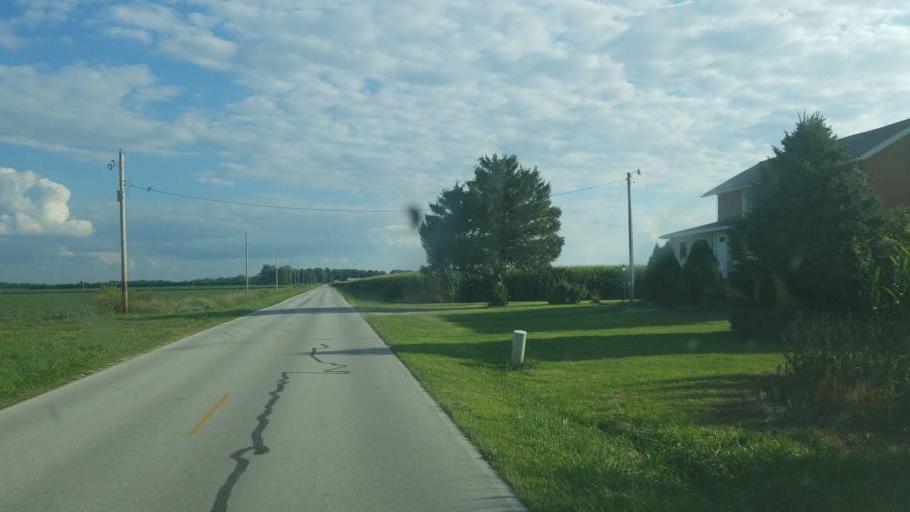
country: US
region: Ohio
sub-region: Sandusky County
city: Green Springs
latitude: 41.2385
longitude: -83.1311
